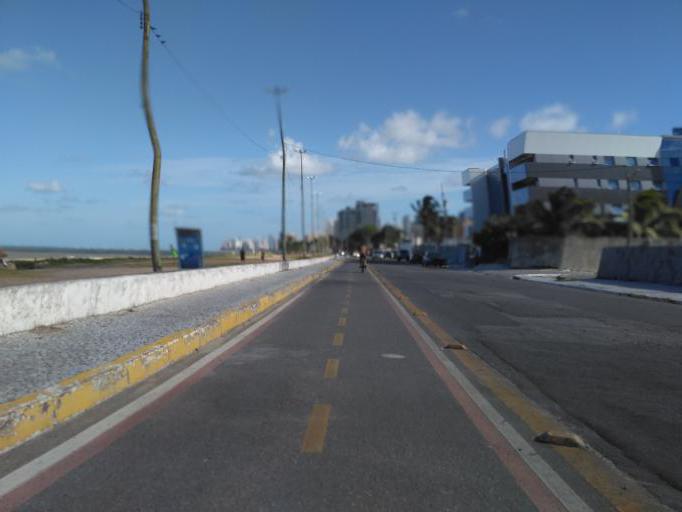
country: BR
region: Pernambuco
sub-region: Jaboatao Dos Guararapes
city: Jaboatao
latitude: -8.1642
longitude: -34.9130
